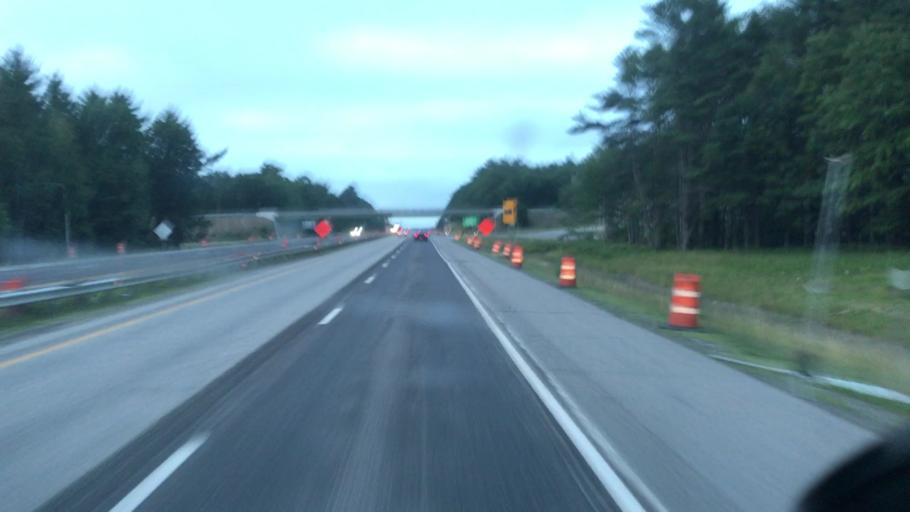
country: US
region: Maine
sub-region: Androscoggin County
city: Auburn
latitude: 44.0468
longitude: -70.2418
